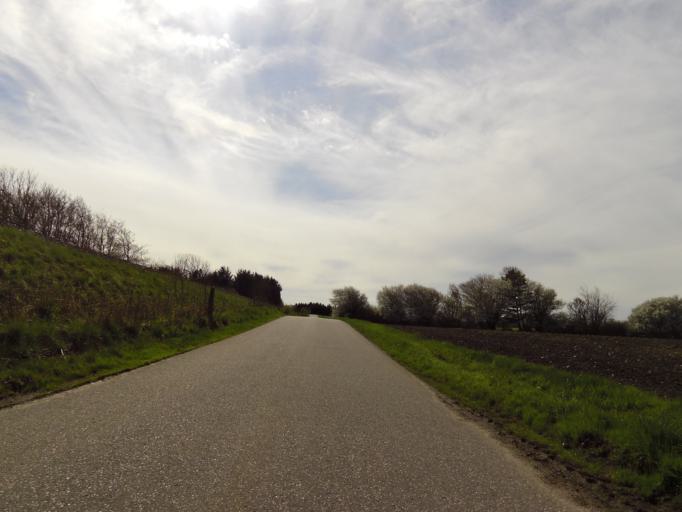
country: DK
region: Central Jutland
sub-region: Skive Kommune
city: Skive
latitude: 56.5595
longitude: 8.9715
